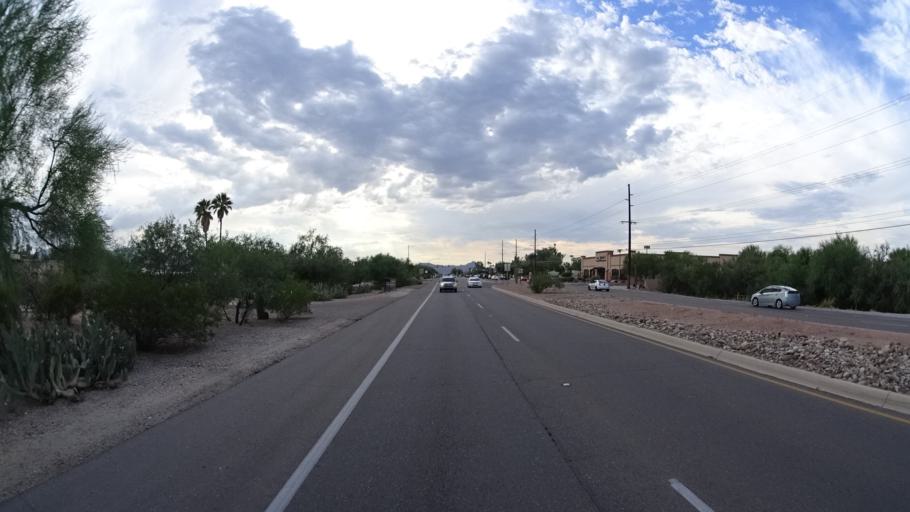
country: US
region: Arizona
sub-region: Pima County
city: Casas Adobes
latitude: 32.3366
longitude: -111.0099
